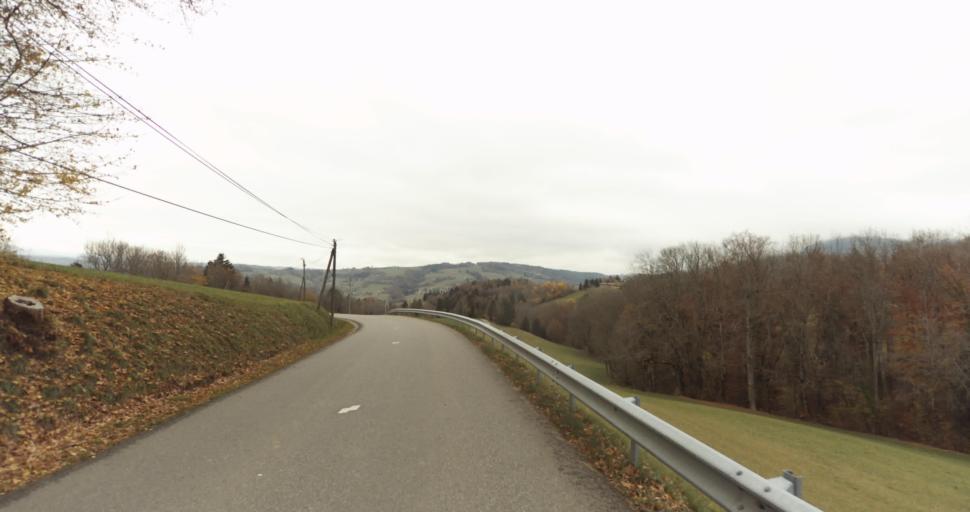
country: FR
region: Rhone-Alpes
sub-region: Departement de la Haute-Savoie
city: Thorens-Glieres
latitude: 45.9799
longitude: 6.2226
